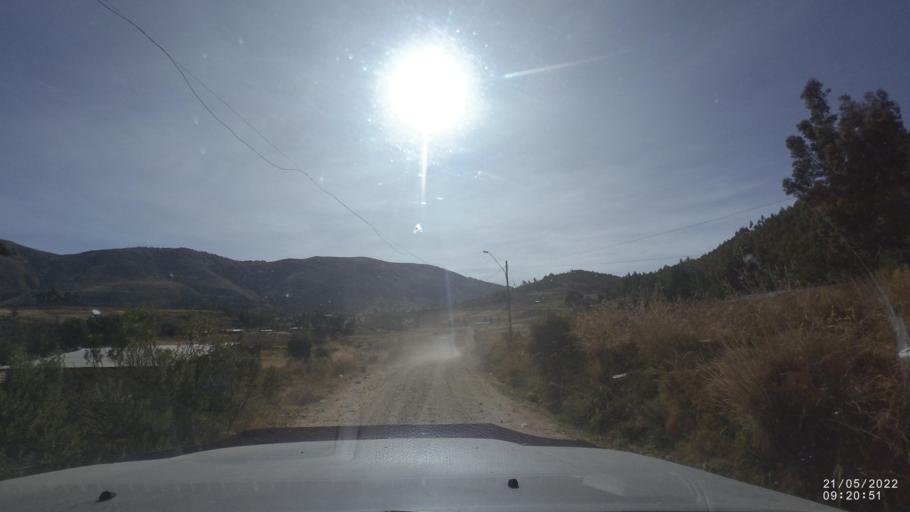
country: BO
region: Cochabamba
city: Cochabamba
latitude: -17.3541
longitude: -66.0194
